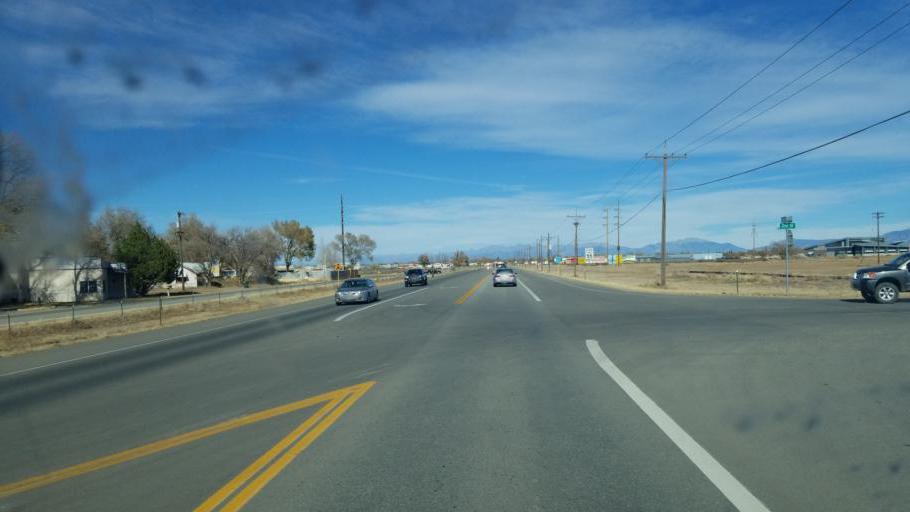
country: US
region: Colorado
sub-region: Alamosa County
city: Alamosa
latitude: 37.4494
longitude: -105.8805
